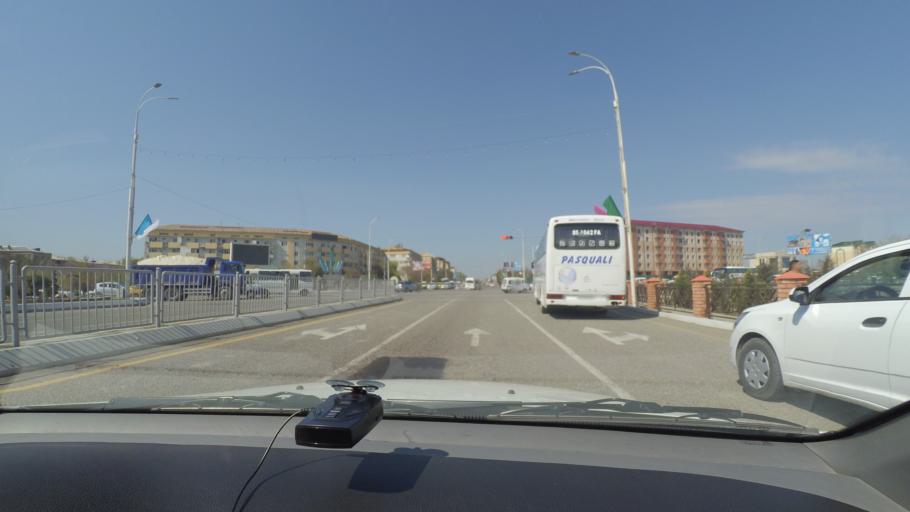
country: UZ
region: Bukhara
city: Bukhara
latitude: 39.7681
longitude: 64.4575
